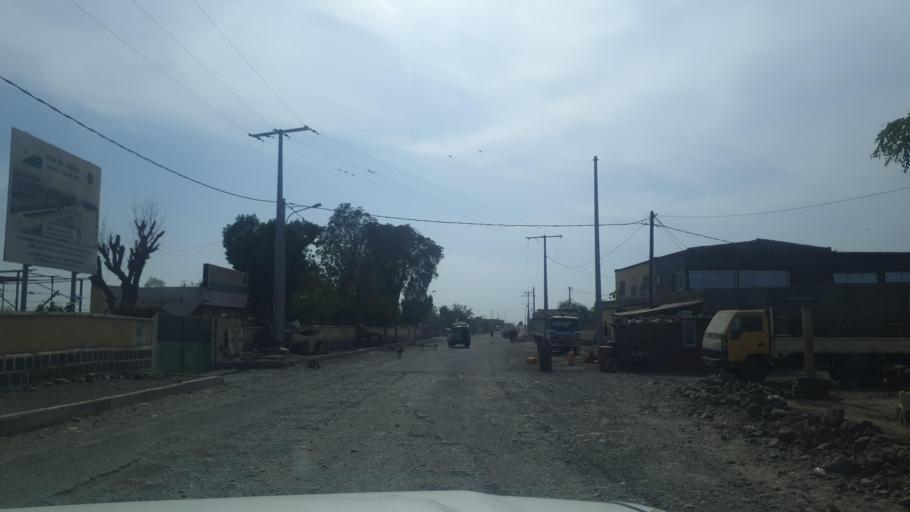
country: DJ
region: Dikhil
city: Dikhil
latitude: 11.1065
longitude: 42.3626
